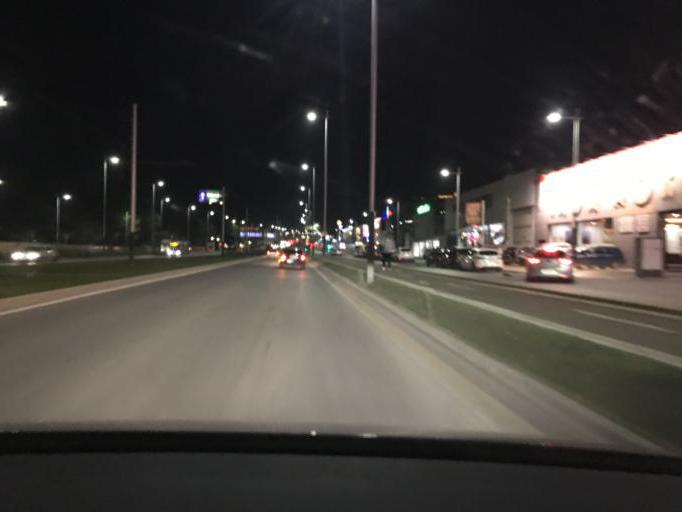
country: ES
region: Andalusia
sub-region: Provincia de Jaen
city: Jaen
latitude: 37.7969
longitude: -3.7794
